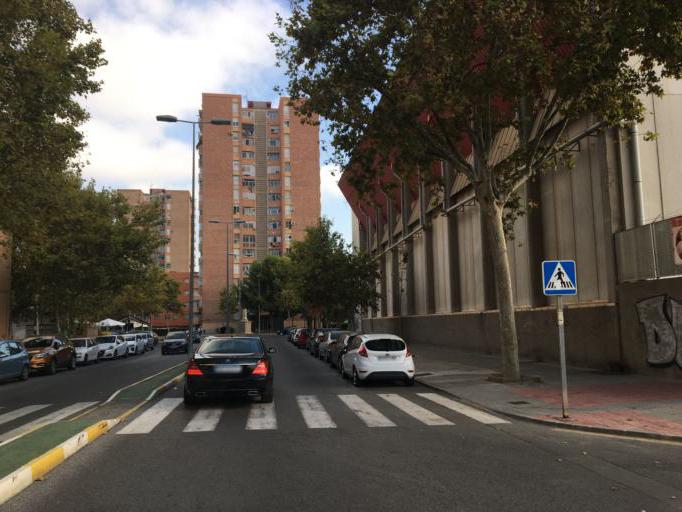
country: ES
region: Murcia
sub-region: Murcia
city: Cartagena
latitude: 37.6080
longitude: -0.9815
